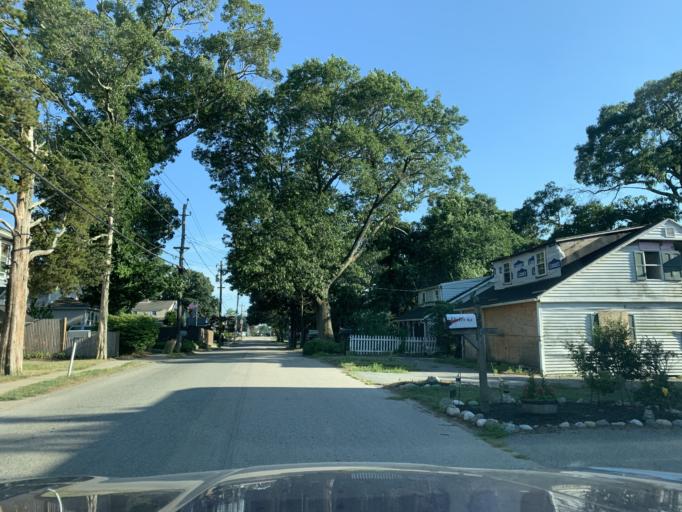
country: US
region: Rhode Island
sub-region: Kent County
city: Warwick
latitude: 41.6916
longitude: -71.4384
